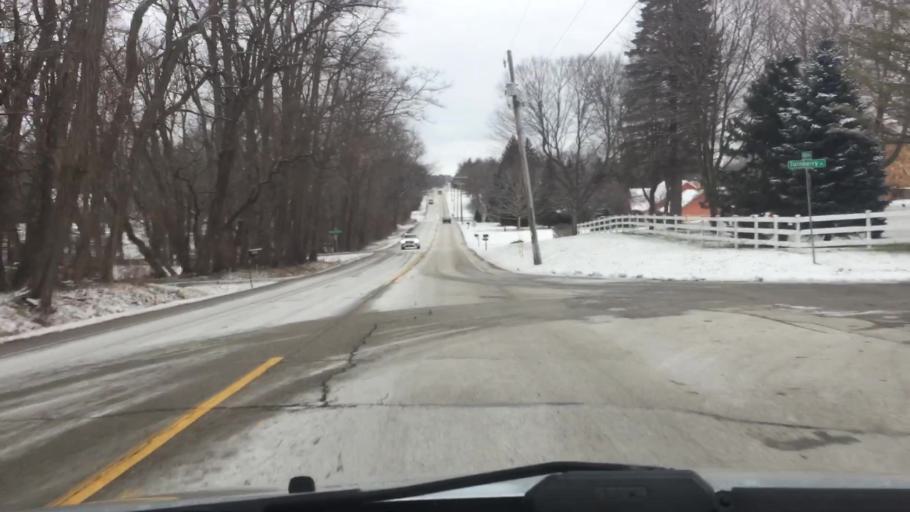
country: US
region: Wisconsin
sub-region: Waukesha County
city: Brookfield
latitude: 43.0825
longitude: -88.1059
